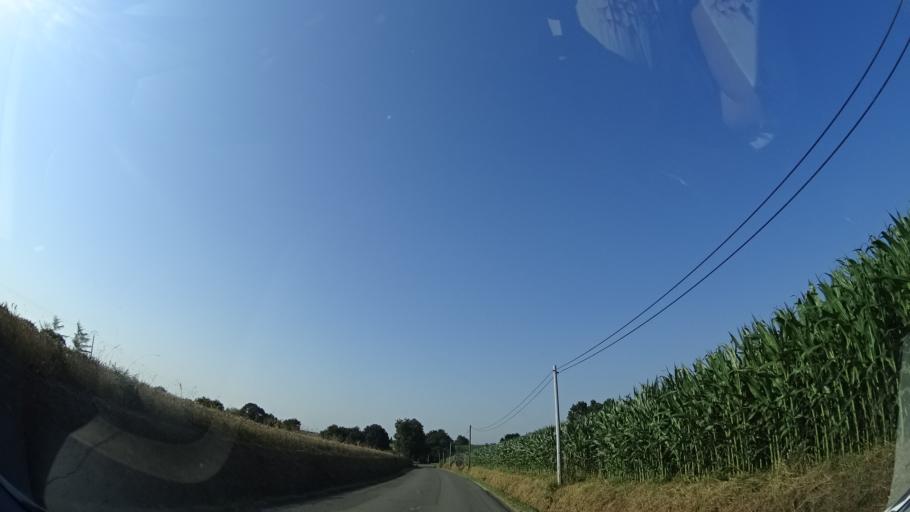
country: FR
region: Brittany
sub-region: Departement d'Ille-et-Vilaine
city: Geveze
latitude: 48.1817
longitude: -1.7942
